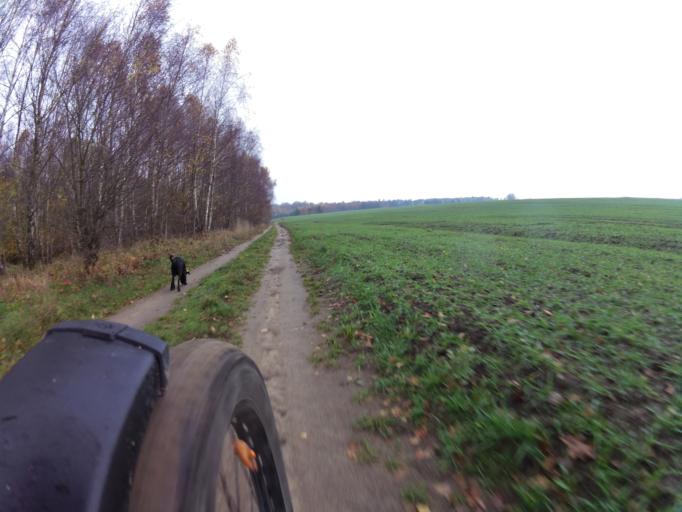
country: PL
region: Pomeranian Voivodeship
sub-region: Powiat pucki
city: Krokowa
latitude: 54.7249
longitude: 18.1324
